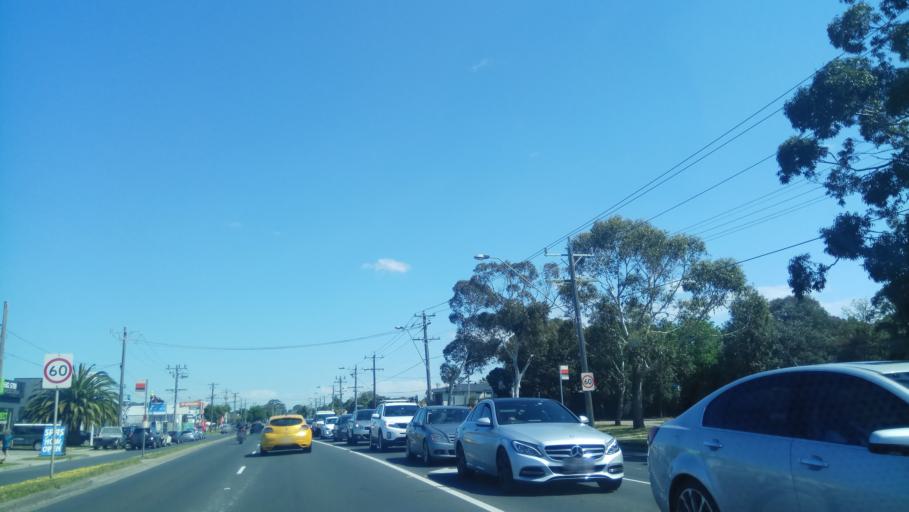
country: AU
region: Victoria
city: Heatherton
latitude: -37.9692
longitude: 145.0869
